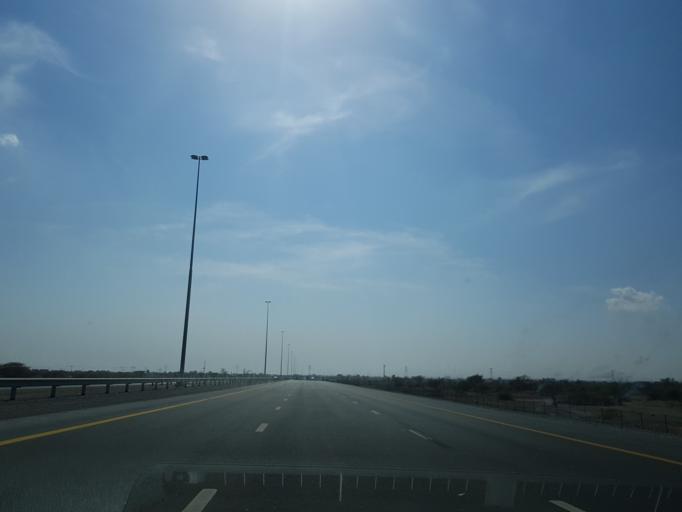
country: AE
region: Ra's al Khaymah
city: Ras al-Khaimah
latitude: 25.7086
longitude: 55.9988
